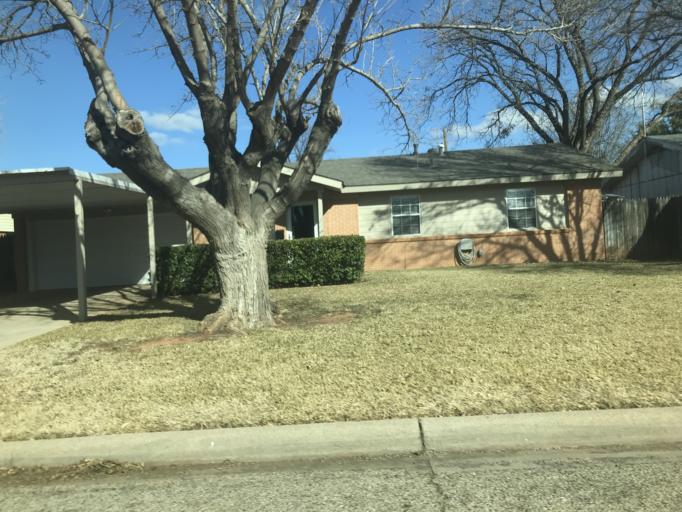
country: US
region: Texas
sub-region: Taylor County
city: Abilene
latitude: 32.4619
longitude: -99.7727
